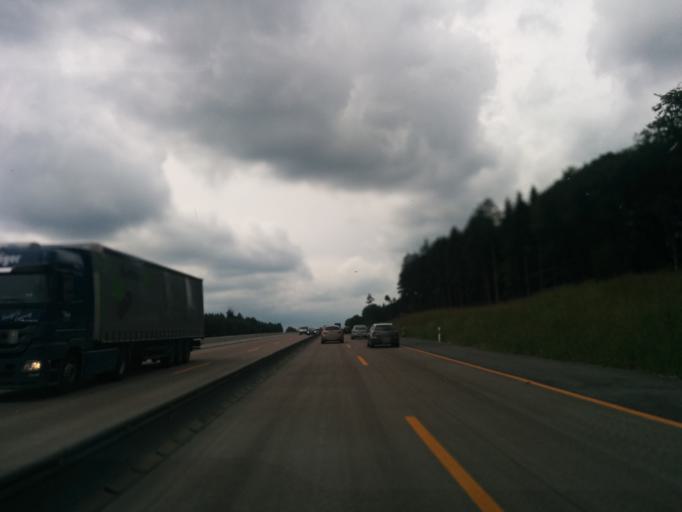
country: DE
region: Bavaria
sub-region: Swabia
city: Aystetten
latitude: 48.4177
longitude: 10.7513
